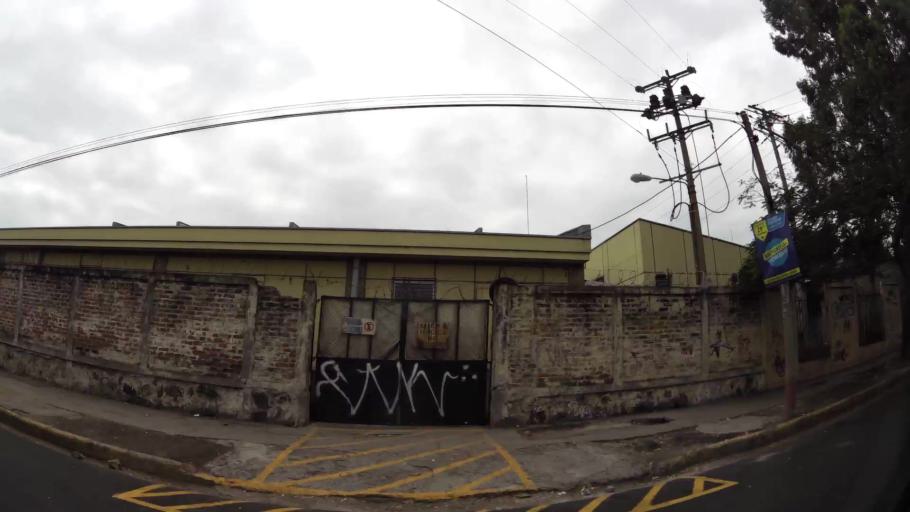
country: SV
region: San Salvador
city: San Salvador
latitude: 13.7016
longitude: -89.2070
